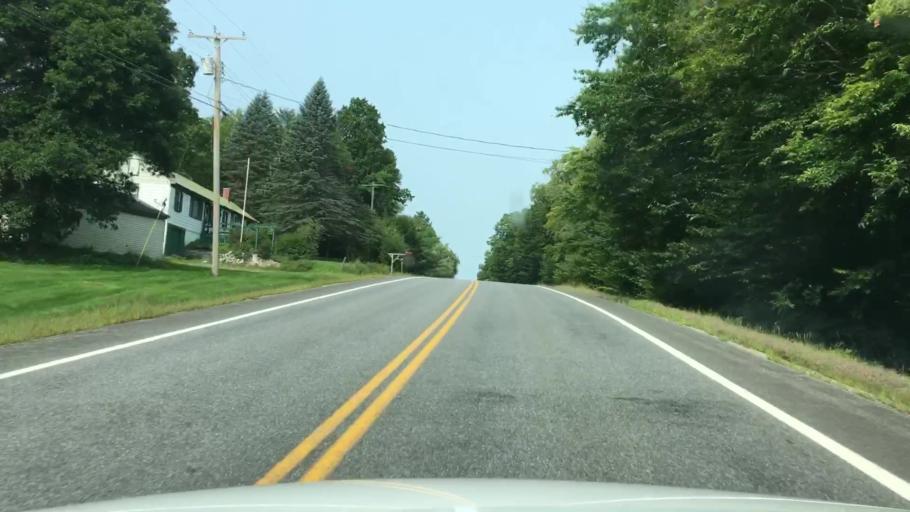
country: US
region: Maine
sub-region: Kennebec County
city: Winthrop
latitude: 44.3272
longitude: -69.9942
